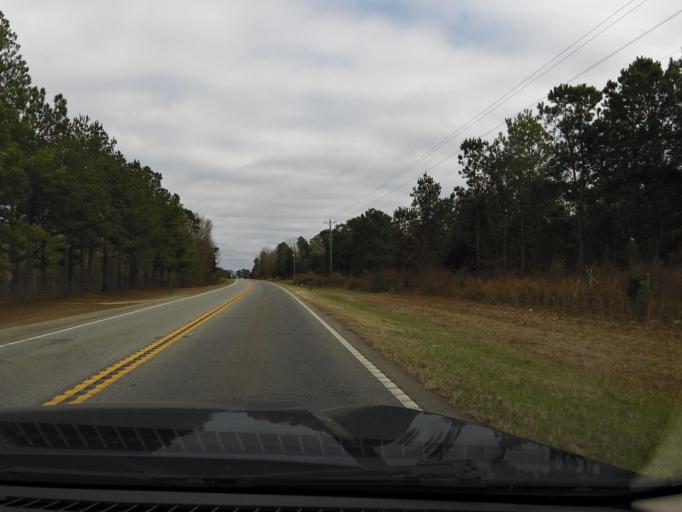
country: US
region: Georgia
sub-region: Quitman County
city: Georgetown
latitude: 31.8580
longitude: -85.0387
